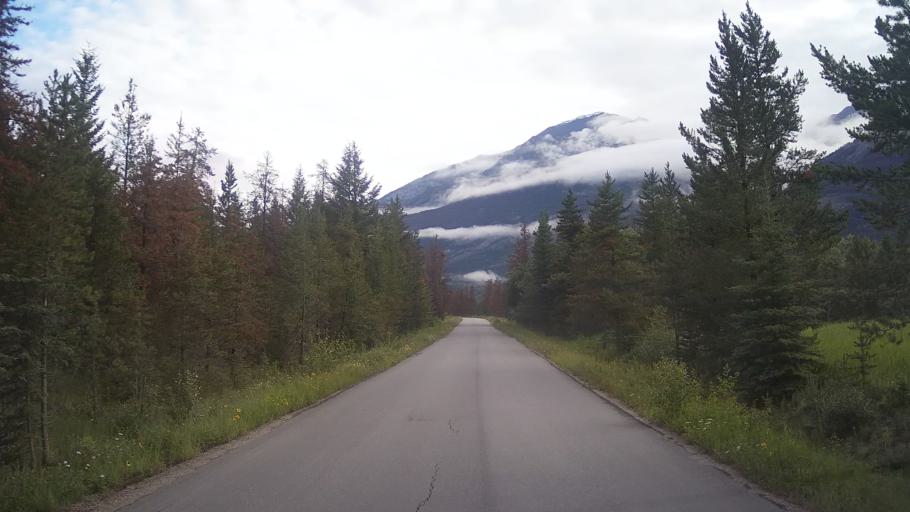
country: CA
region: Alberta
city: Jasper Park Lodge
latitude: 52.9658
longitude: -118.0601
